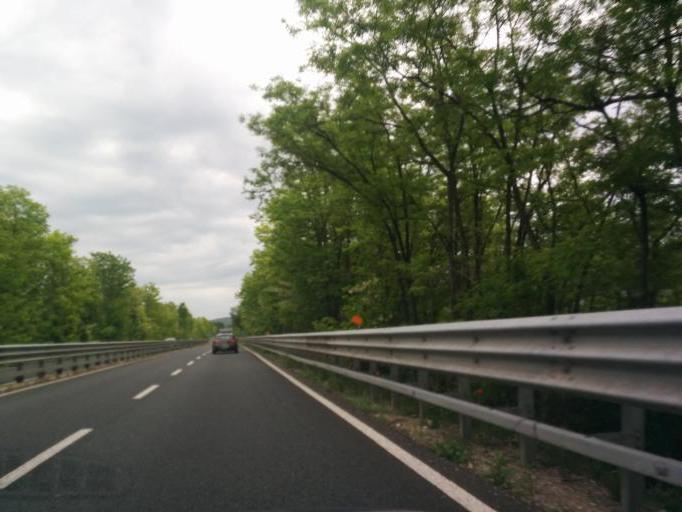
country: IT
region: Tuscany
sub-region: Provincia di Siena
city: Staggia
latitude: 43.4034
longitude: 11.1862
